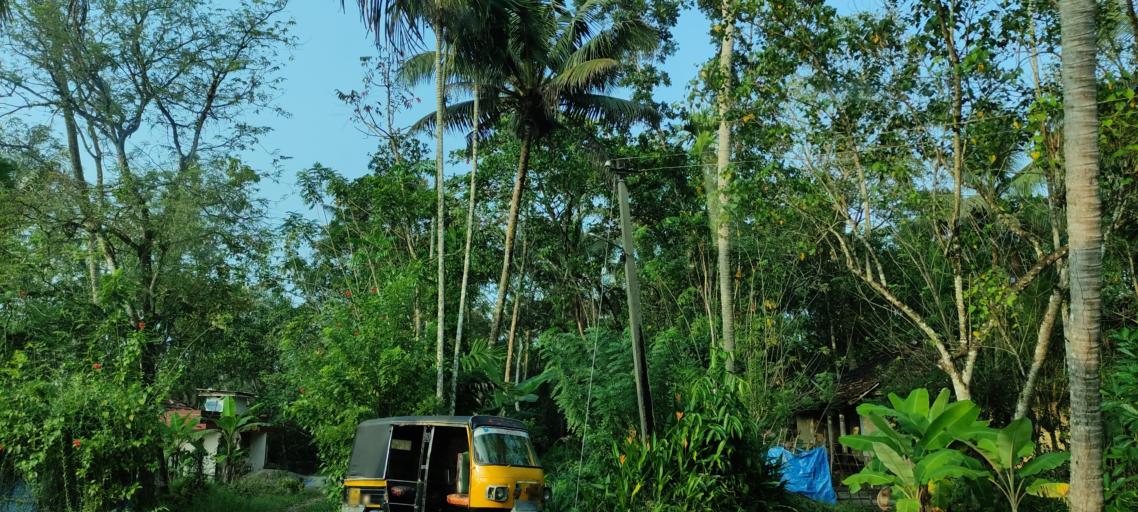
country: IN
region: Kerala
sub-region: Alappuzha
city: Shertallai
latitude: 9.6684
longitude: 76.3579
